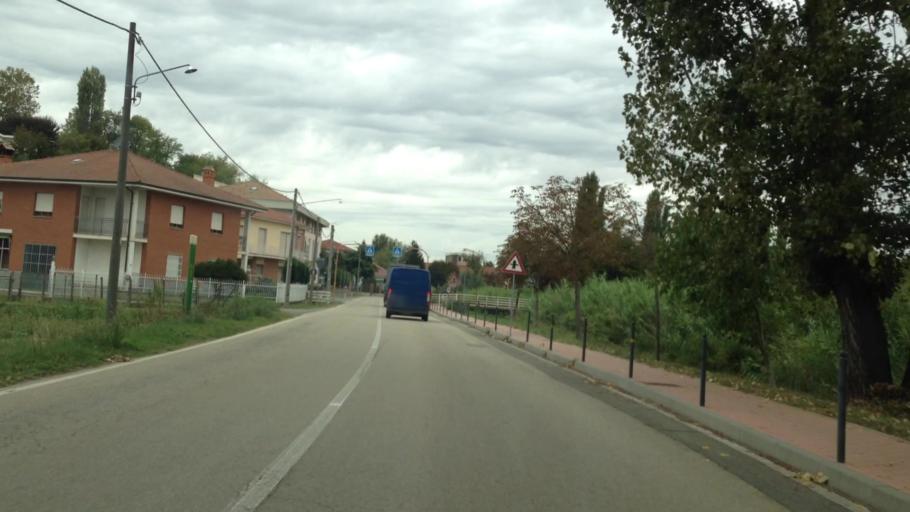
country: IT
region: Piedmont
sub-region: Provincia di Alessandria
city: Quattordio
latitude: 44.8993
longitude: 8.4092
